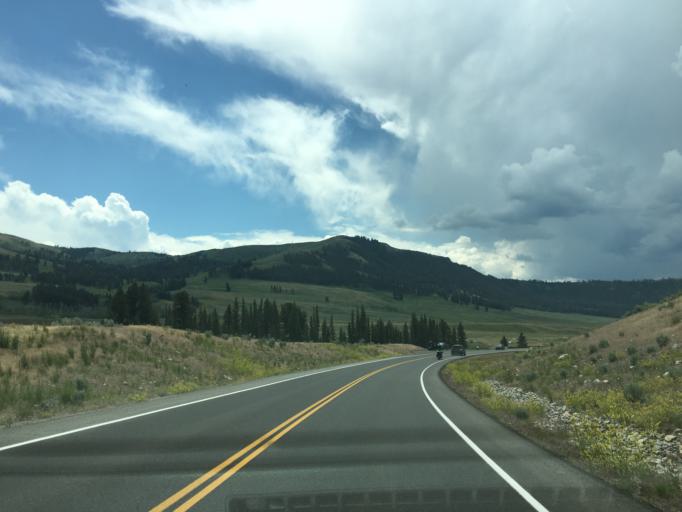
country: US
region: Montana
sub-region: Park County
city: Livingston
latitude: 44.9168
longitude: -110.3211
